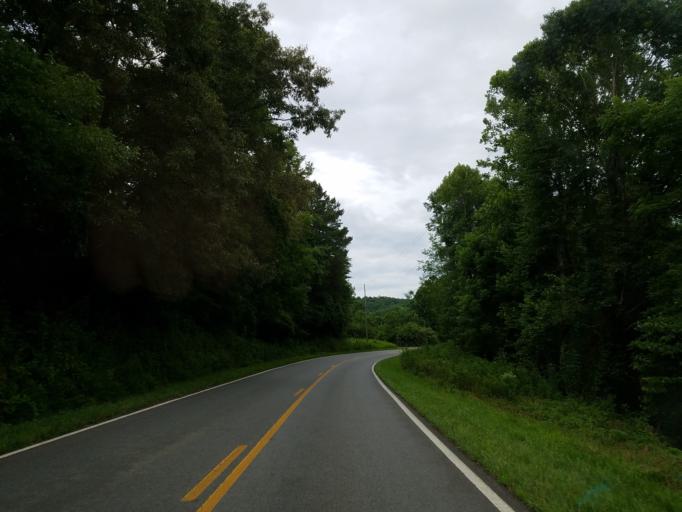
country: US
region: Georgia
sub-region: Gilmer County
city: Ellijay
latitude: 34.6698
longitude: -84.3838
